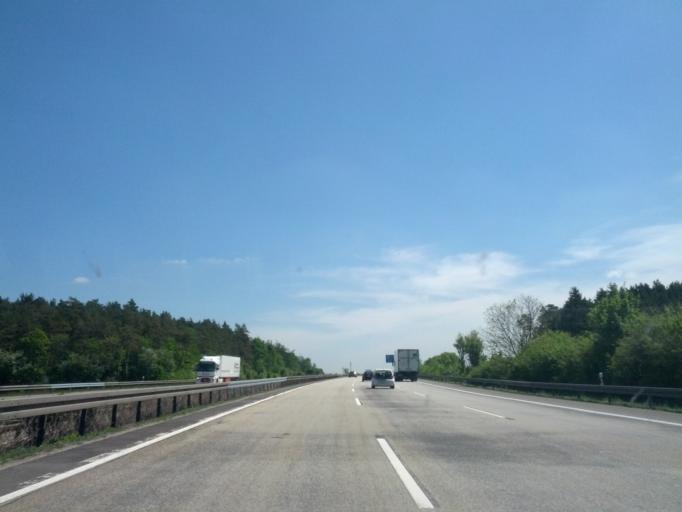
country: DE
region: Thuringia
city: Troistedt
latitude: 50.9475
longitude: 11.2765
